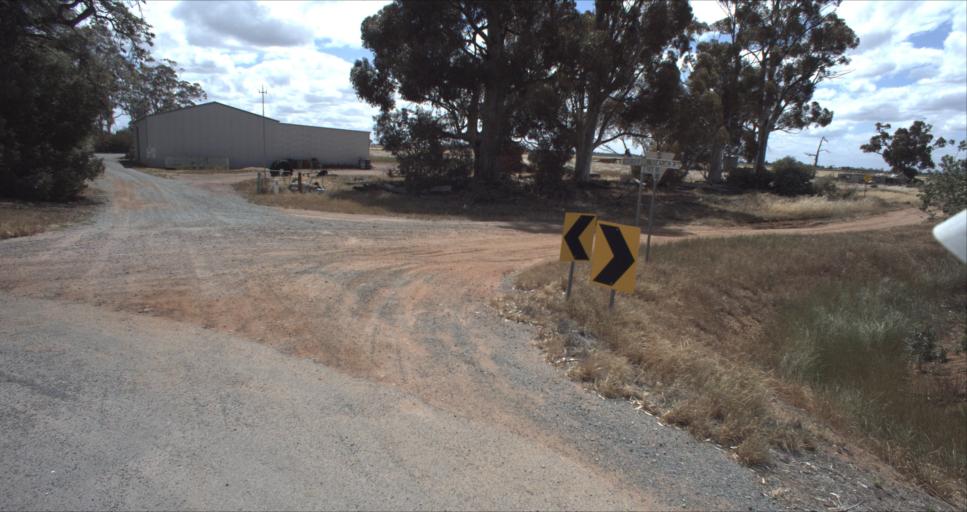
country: AU
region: New South Wales
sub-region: Leeton
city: Leeton
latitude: -34.5870
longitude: 146.3718
